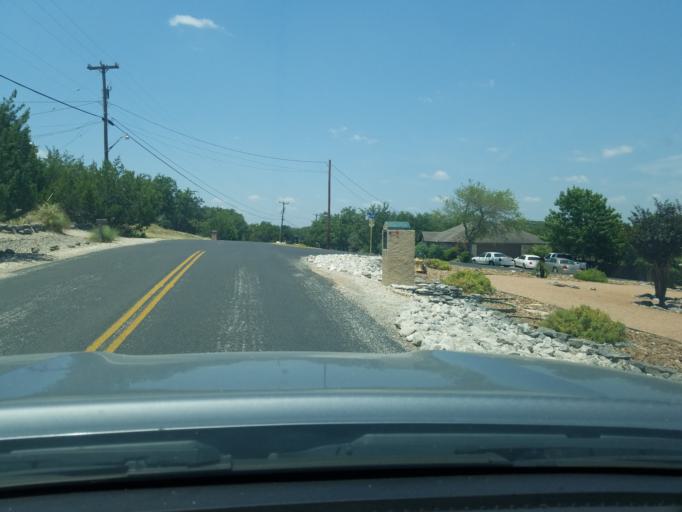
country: US
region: Texas
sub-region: Bexar County
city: Timberwood Park
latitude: 29.6949
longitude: -98.4857
